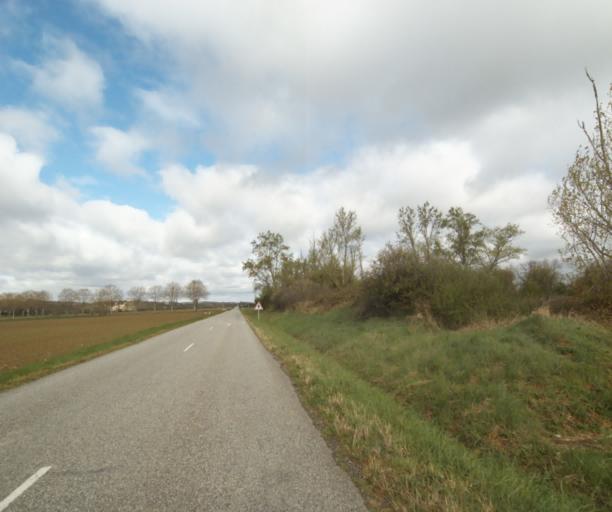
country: FR
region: Midi-Pyrenees
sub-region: Departement de l'Ariege
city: Saverdun
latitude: 43.2503
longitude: 1.5515
